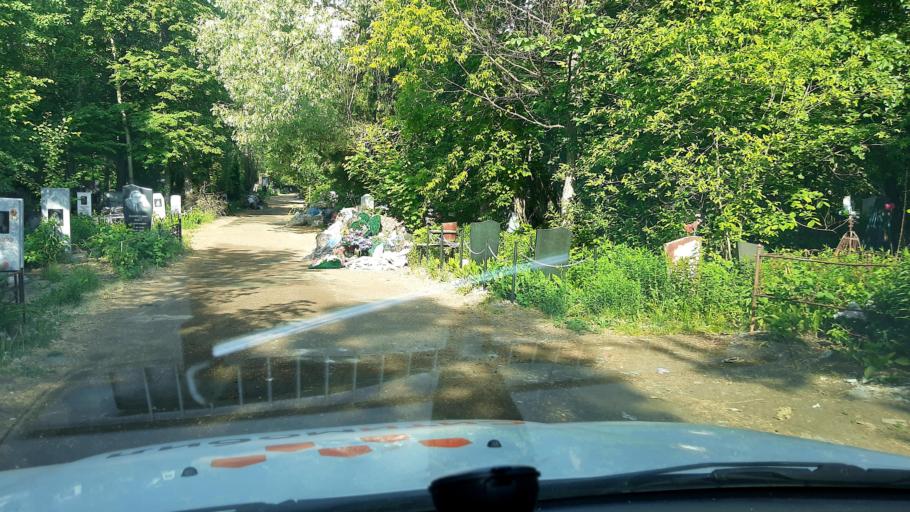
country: RU
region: Bashkortostan
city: Mikhaylovka
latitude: 54.8093
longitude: 55.8675
